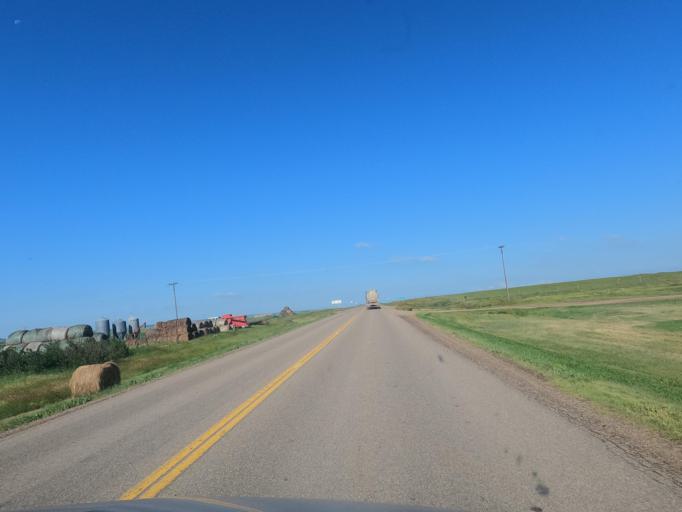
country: CA
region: Saskatchewan
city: Swift Current
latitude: 49.7278
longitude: -107.7450
